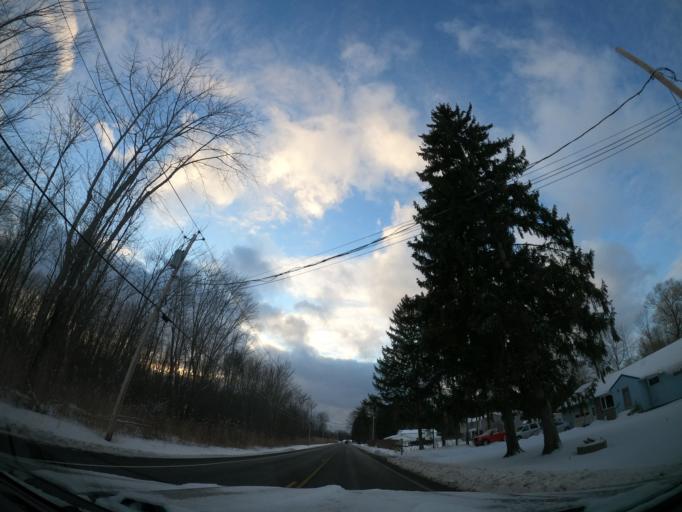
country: US
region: New York
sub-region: Onondaga County
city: Brewerton
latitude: 43.2167
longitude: -76.1464
